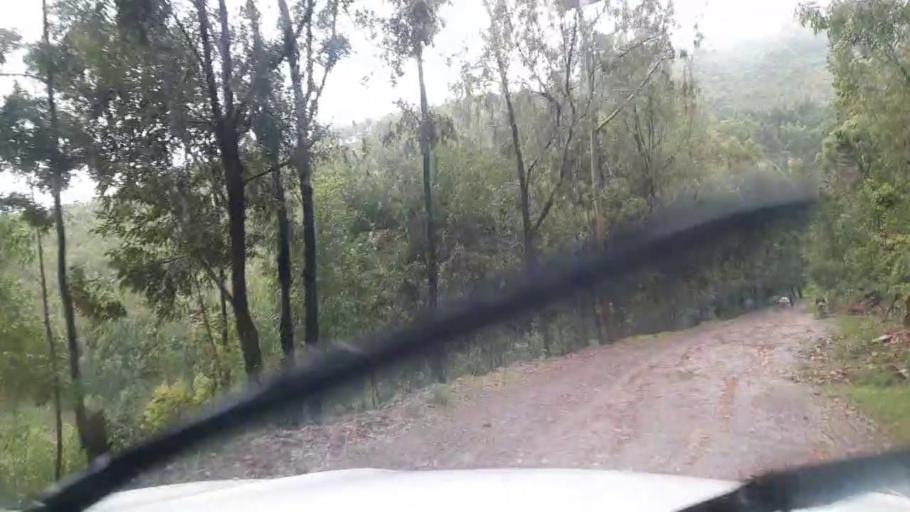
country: RW
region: Northern Province
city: Byumba
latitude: -1.7613
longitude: 29.9918
